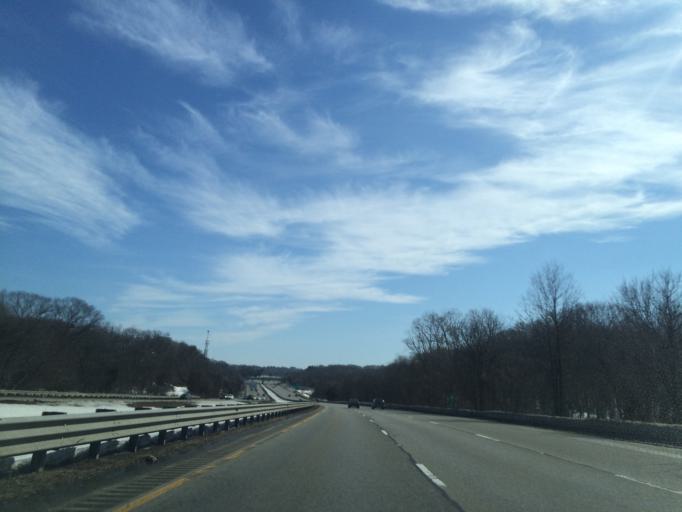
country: US
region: Massachusetts
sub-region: Middlesex County
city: Lexington
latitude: 42.4181
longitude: -71.2145
